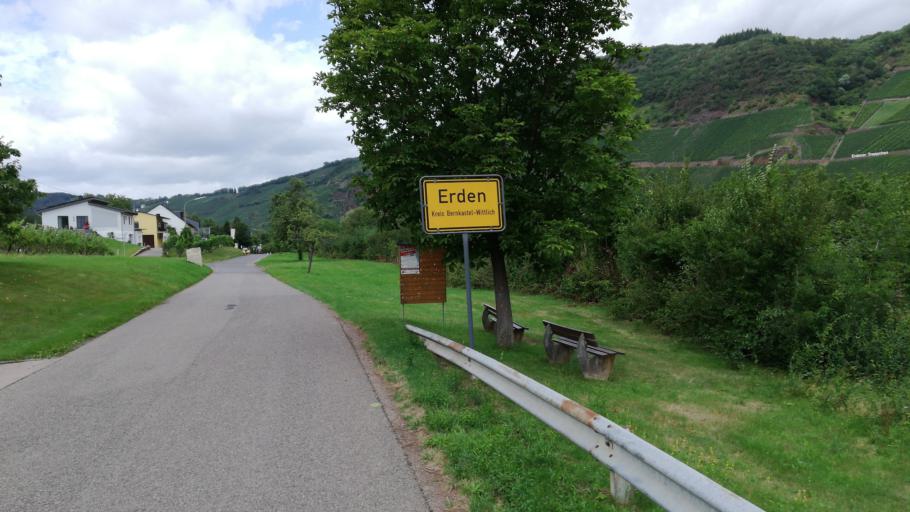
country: DE
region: Rheinland-Pfalz
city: Losnich
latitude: 49.9779
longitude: 7.0328
